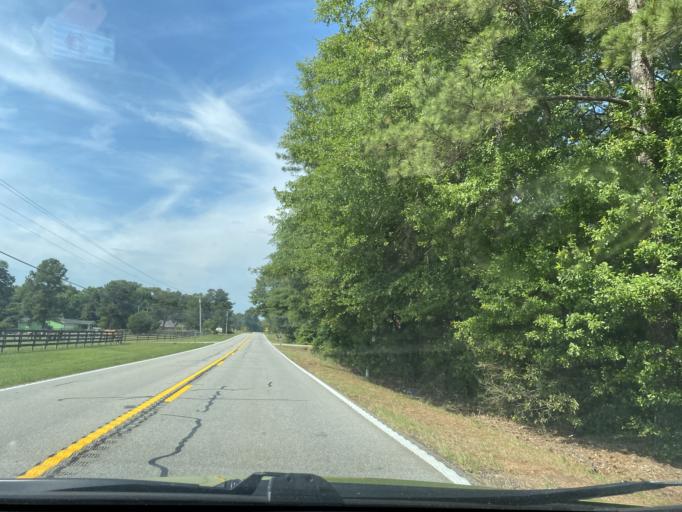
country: US
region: Georgia
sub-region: Coweta County
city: East Newnan
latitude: 33.2650
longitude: -84.7192
